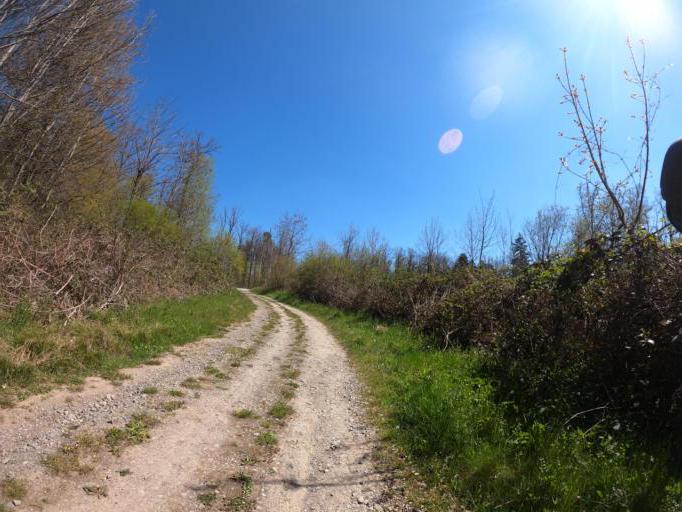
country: DE
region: Baden-Wuerttemberg
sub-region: Karlsruhe Region
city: Eutingen
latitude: 48.8867
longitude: 8.7405
